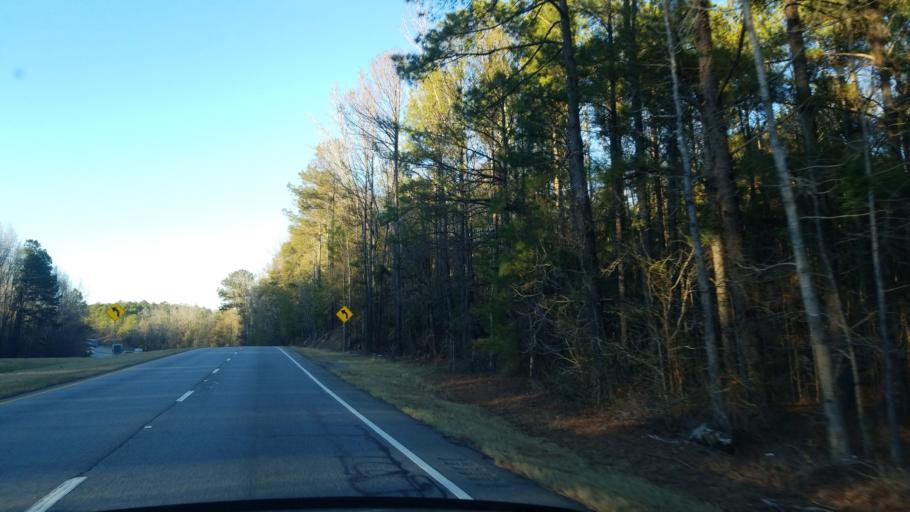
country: US
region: Georgia
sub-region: Chattahoochee County
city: Cusseta
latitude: 32.2497
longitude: -84.7200
